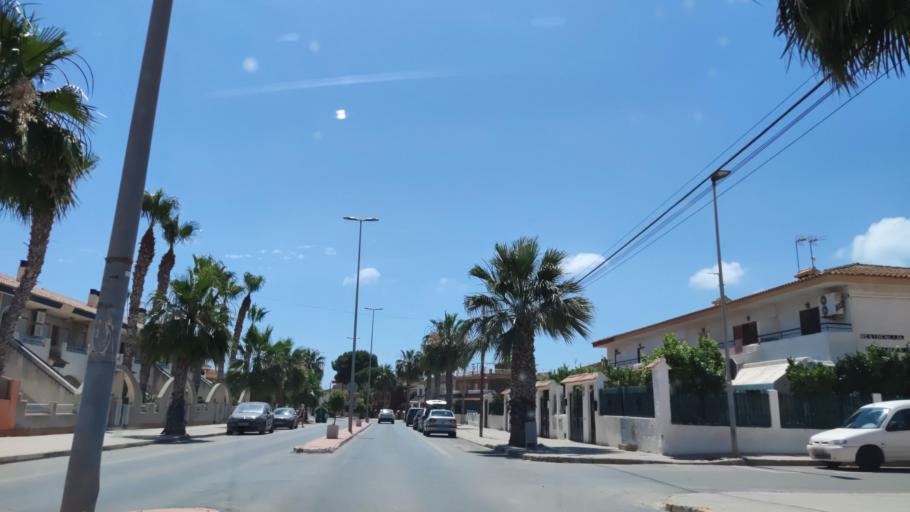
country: ES
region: Murcia
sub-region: Murcia
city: Los Alcazares
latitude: 37.7583
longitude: -0.8372
